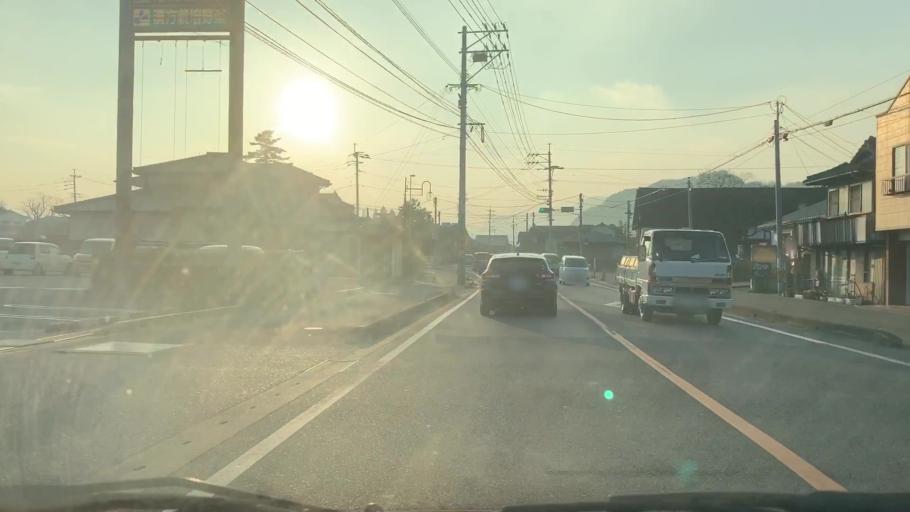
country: JP
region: Saga Prefecture
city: Takeocho-takeo
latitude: 33.2618
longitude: 130.0898
